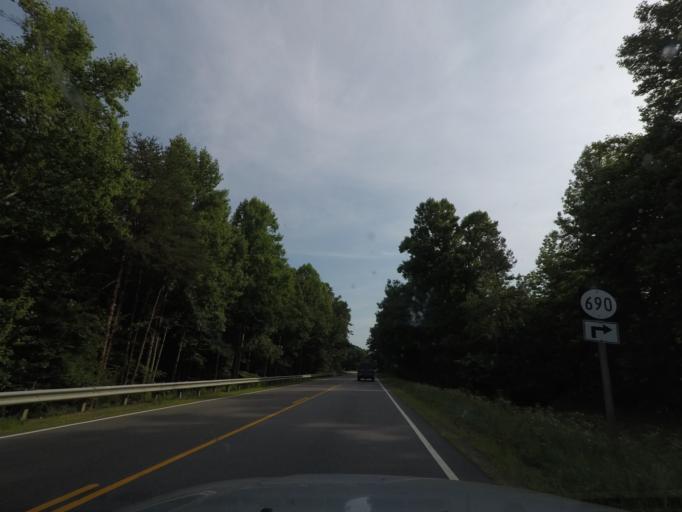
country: US
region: Virginia
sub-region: Mecklenburg County
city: Chase City
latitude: 36.8051
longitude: -78.6027
